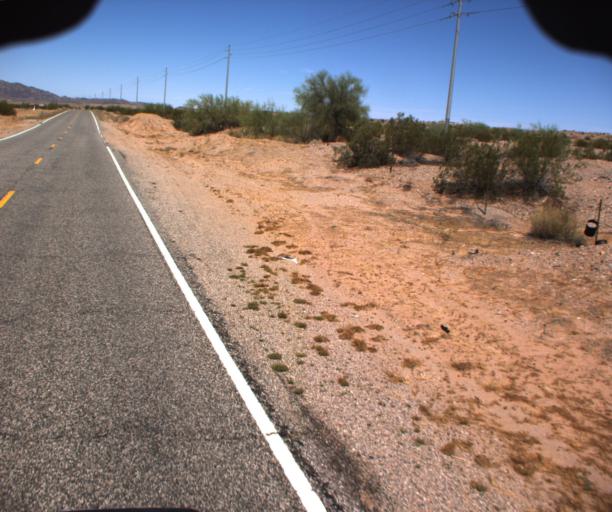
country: US
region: Arizona
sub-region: La Paz County
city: Parker
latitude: 33.9951
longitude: -114.1766
